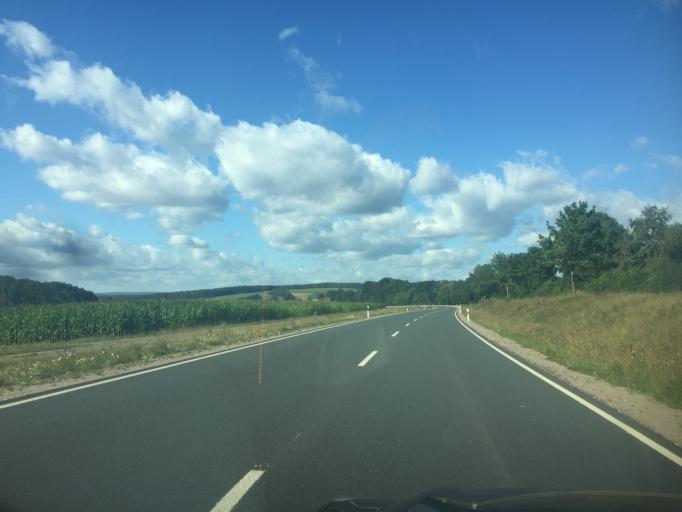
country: DE
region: Bavaria
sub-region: Upper Palatinate
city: Gebenbach
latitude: 49.5497
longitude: 11.8659
